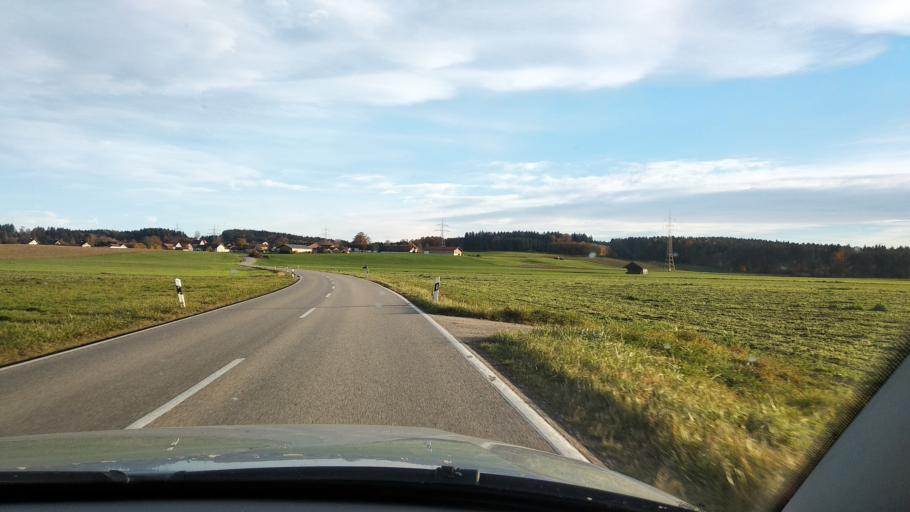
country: DE
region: Bavaria
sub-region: Upper Bavaria
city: Zorneding
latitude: 48.0654
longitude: 11.8427
